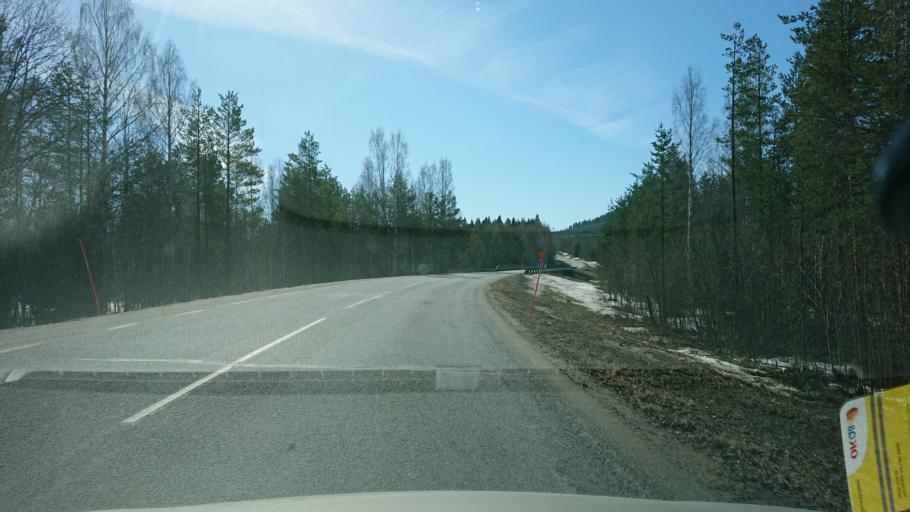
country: SE
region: Vaesterbotten
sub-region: Dorotea Kommun
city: Dorotea
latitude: 64.0061
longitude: 16.3053
